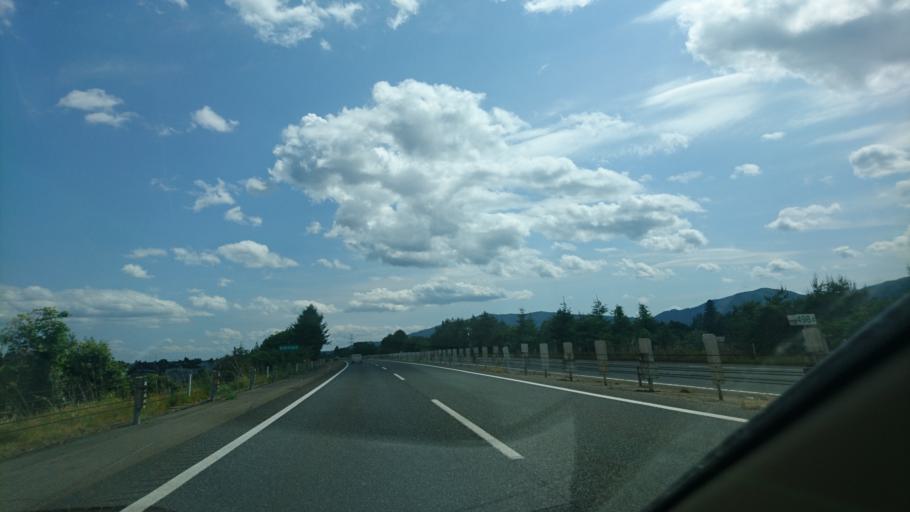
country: JP
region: Iwate
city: Morioka-shi
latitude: 39.5954
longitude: 141.1185
